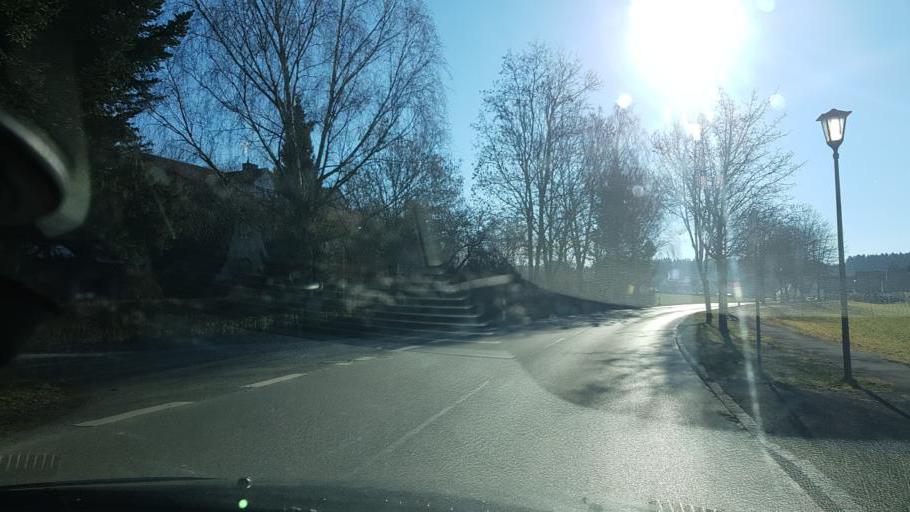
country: DE
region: Bavaria
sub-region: Upper Bavaria
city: Oberschweinbach
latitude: 48.2377
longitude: 11.1569
